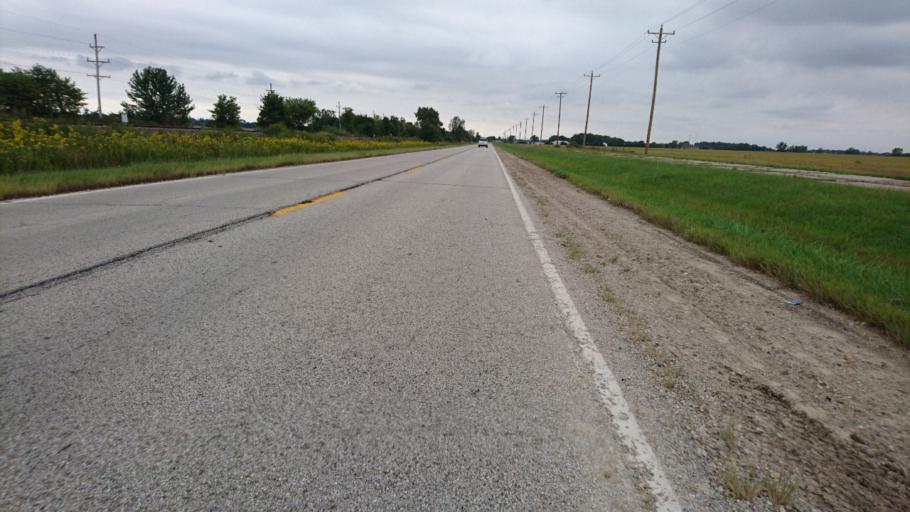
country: US
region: Illinois
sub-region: Livingston County
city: Pontiac
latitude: 40.9088
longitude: -88.6134
